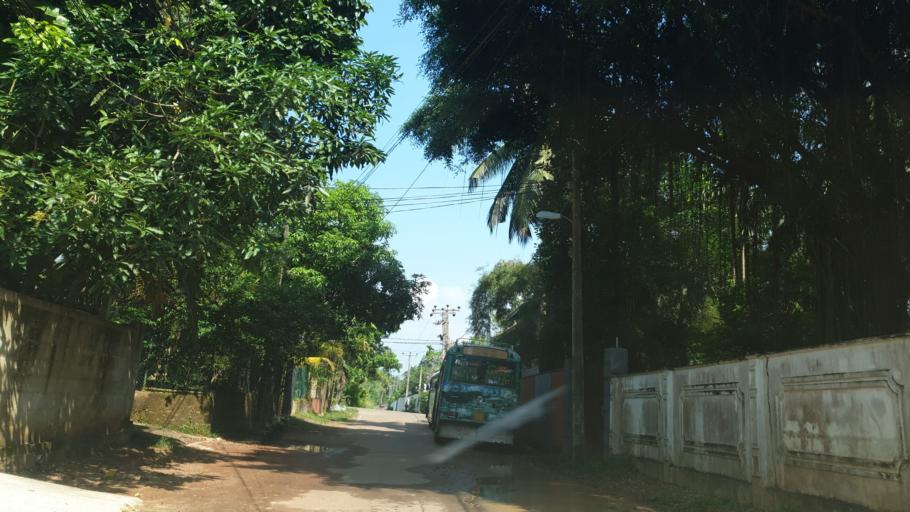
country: LK
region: Western
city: Moratuwa
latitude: 6.7600
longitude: 79.9239
